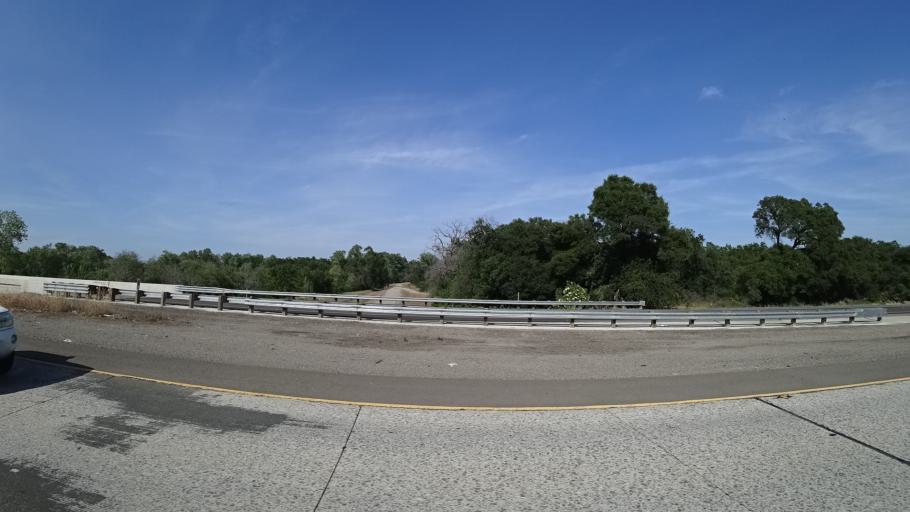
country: US
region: California
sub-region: Butte County
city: Durham
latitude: 39.6938
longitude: -121.7778
